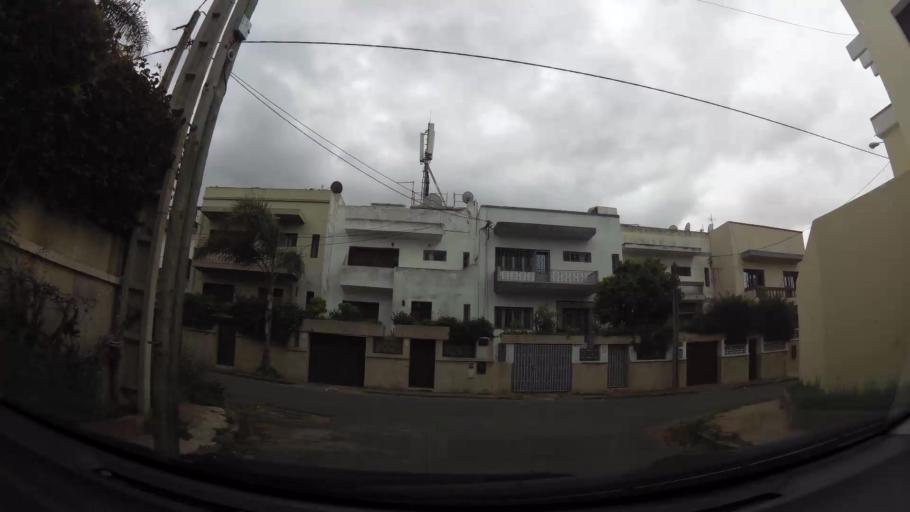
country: MA
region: Grand Casablanca
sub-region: Casablanca
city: Casablanca
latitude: 33.5768
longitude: -7.6696
